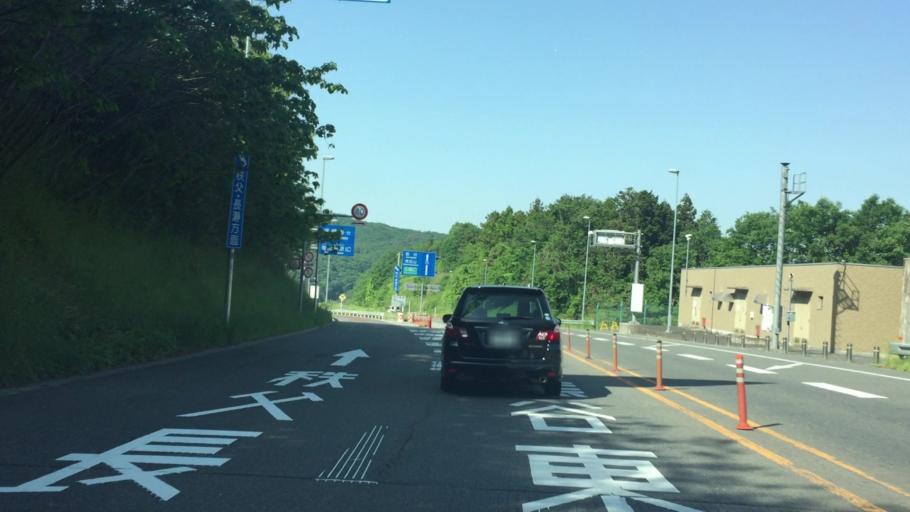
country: JP
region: Saitama
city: Yorii
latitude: 36.1097
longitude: 139.1681
